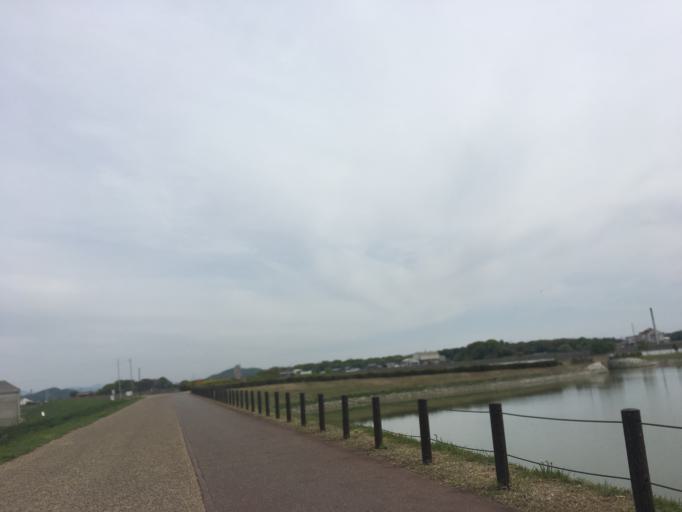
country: JP
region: Hyogo
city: Miki
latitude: 34.7666
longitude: 134.9211
